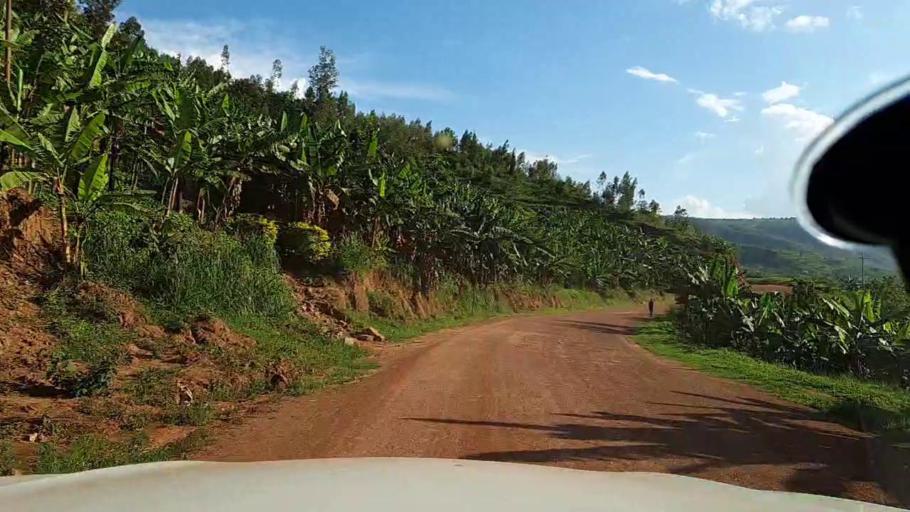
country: RW
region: Kigali
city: Kigali
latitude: -1.8679
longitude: 29.9318
